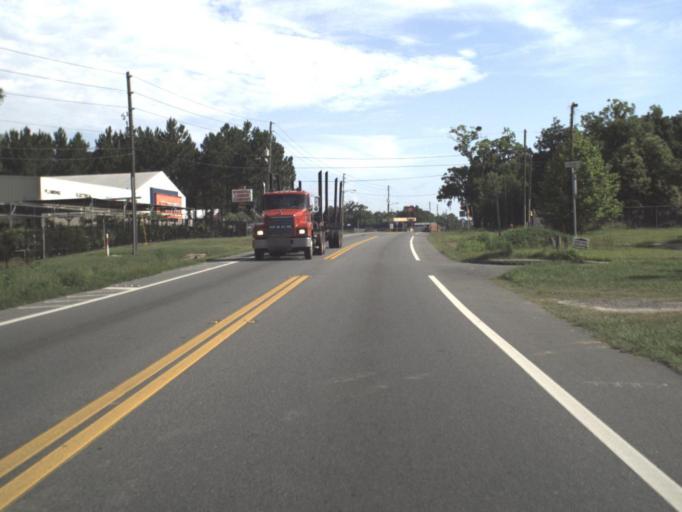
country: US
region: Florida
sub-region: Madison County
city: Madison
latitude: 30.4598
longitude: -83.4097
